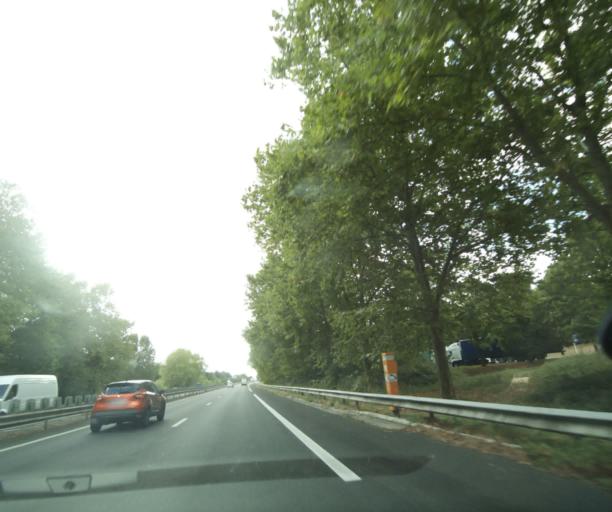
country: FR
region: Poitou-Charentes
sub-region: Departement de la Charente-Maritime
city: Chermignac
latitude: 45.7048
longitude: -0.6521
